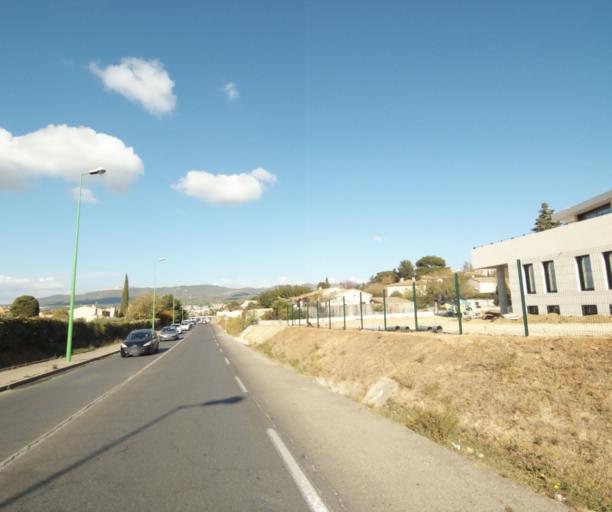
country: FR
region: Provence-Alpes-Cote d'Azur
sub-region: Departement des Bouches-du-Rhone
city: Allauch
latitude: 43.3395
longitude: 5.4739
